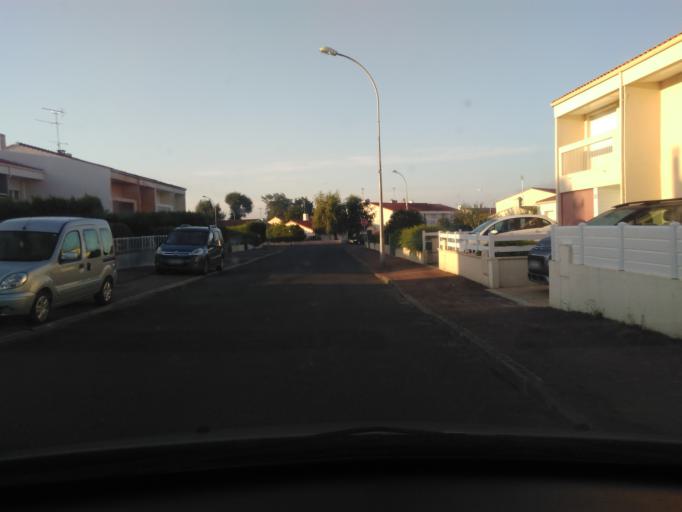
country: FR
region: Pays de la Loire
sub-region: Departement de la Vendee
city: Mouilleron-le-Captif
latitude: 46.7272
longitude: -1.4217
